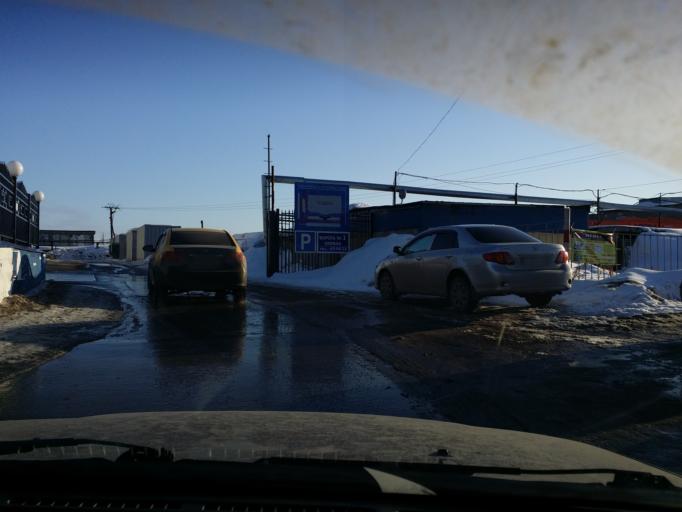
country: RU
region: Khanty-Mansiyskiy Avtonomnyy Okrug
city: Nizhnevartovsk
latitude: 60.9300
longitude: 76.5275
